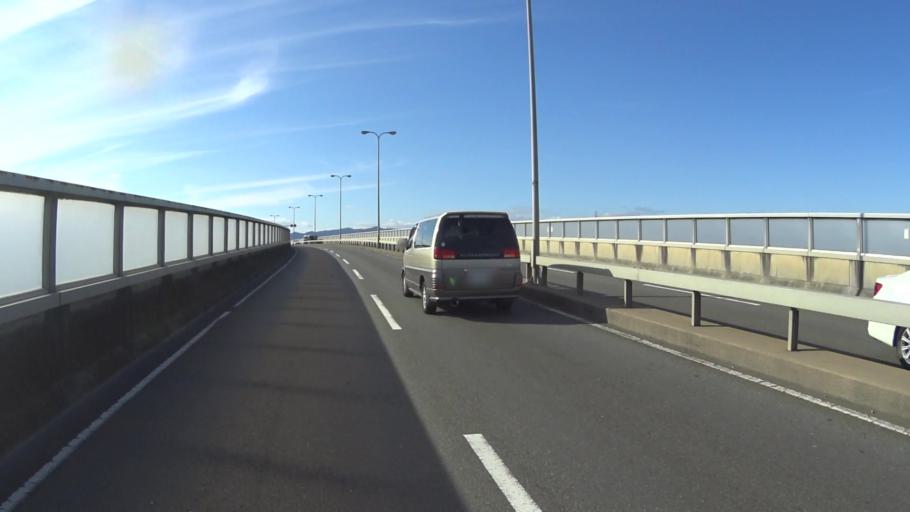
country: JP
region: Kyoto
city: Muko
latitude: 34.9292
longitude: 135.7355
